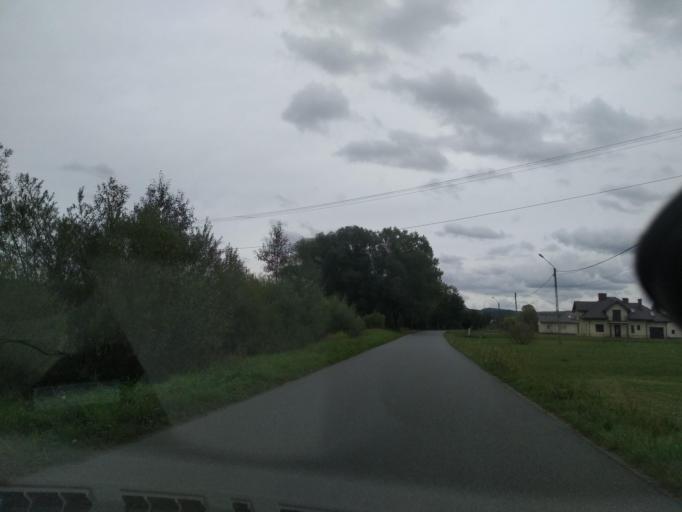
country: PL
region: Subcarpathian Voivodeship
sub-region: Powiat krosnienski
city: Dukla
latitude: 49.5511
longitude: 21.7016
